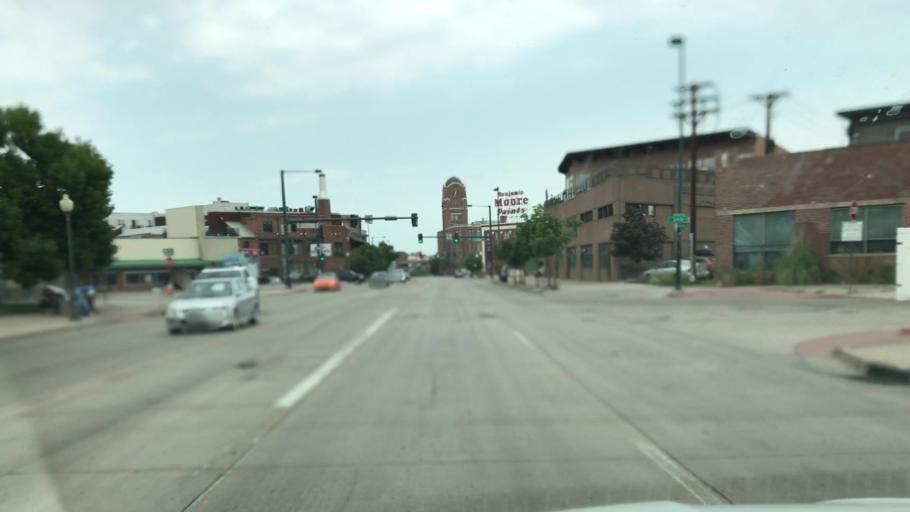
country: US
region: Colorado
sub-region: Denver County
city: Denver
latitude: 39.7561
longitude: -104.9874
